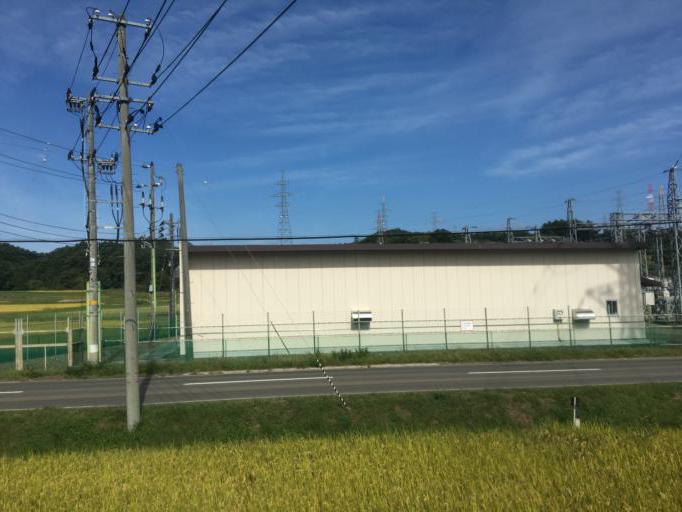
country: JP
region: Iwate
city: Morioka-shi
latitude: 39.8980
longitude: 141.1605
